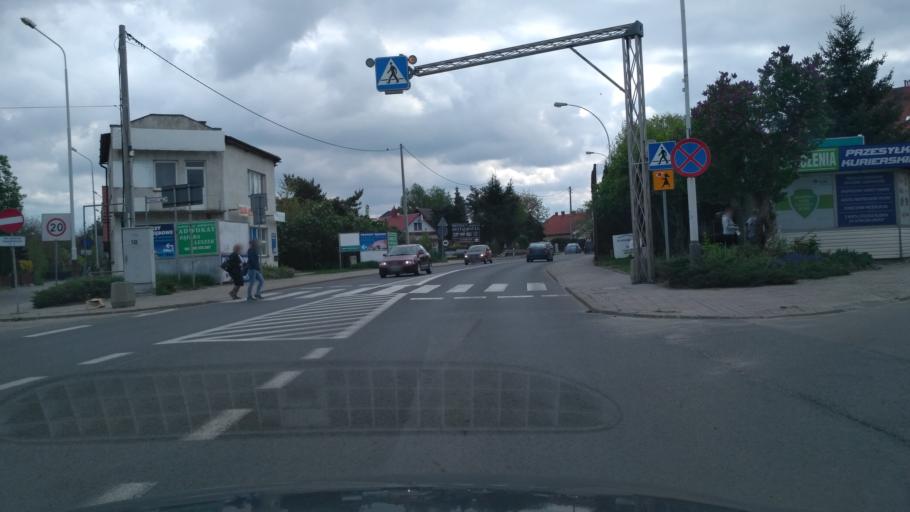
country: PL
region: Subcarpathian Voivodeship
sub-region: Powiat przeworski
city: Przeworsk
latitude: 50.0589
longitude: 22.4952
